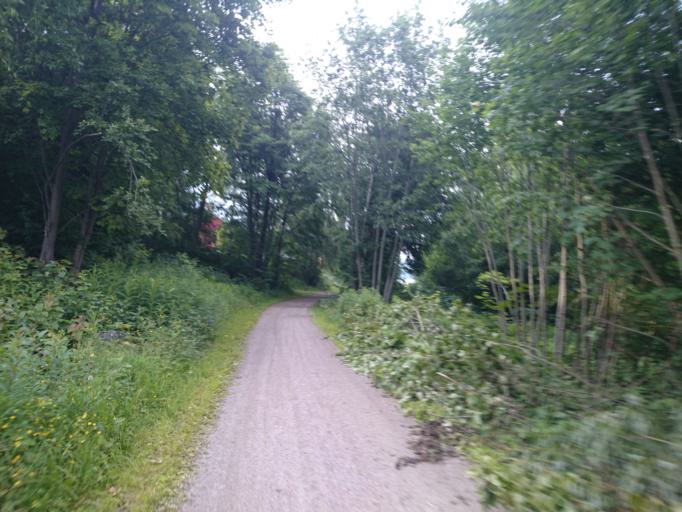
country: SE
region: Vaesternorrland
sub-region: Sundsvalls Kommun
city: Stockvik
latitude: 62.3255
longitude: 17.3702
